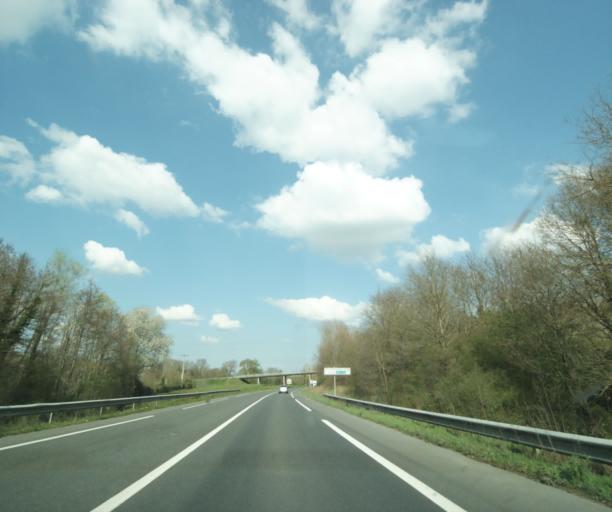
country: FR
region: Auvergne
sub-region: Departement de l'Allier
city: Bessay-sur-Allier
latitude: 46.4731
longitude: 3.3040
